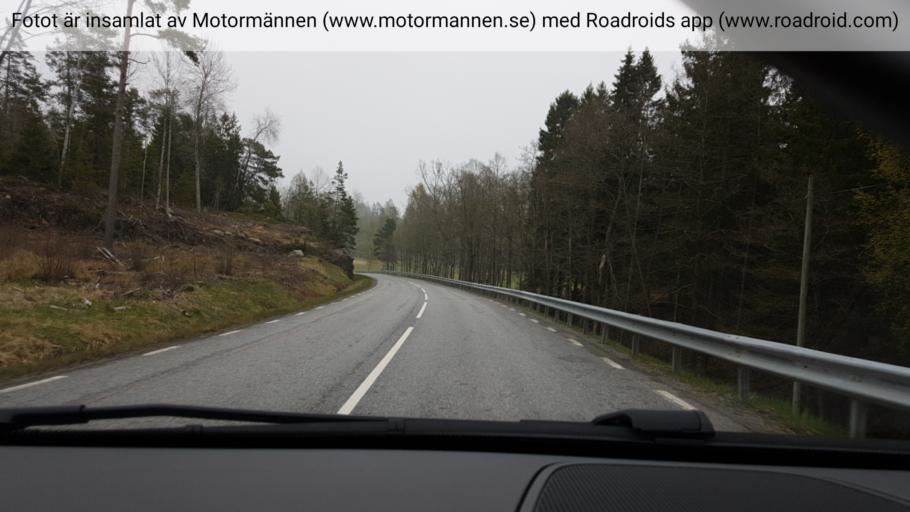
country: SE
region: Stockholm
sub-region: Nynashamns Kommun
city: Osmo
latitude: 58.9692
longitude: 17.9424
